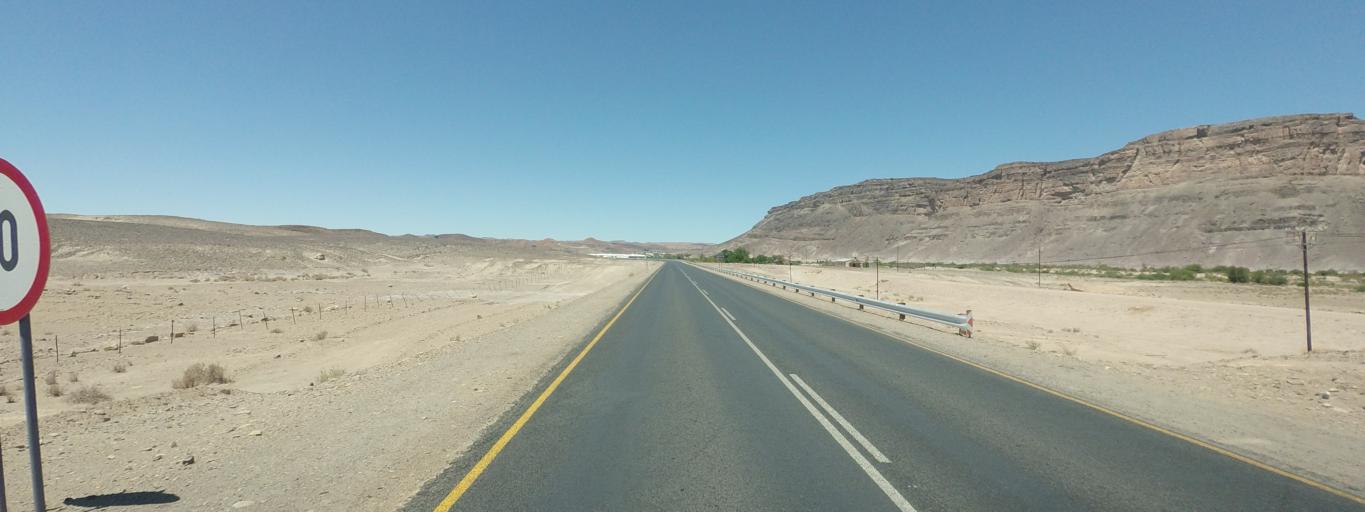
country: ZA
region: Northern Cape
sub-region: Namakwa District Municipality
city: Port Nolloth
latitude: -28.7504
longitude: 17.6191
